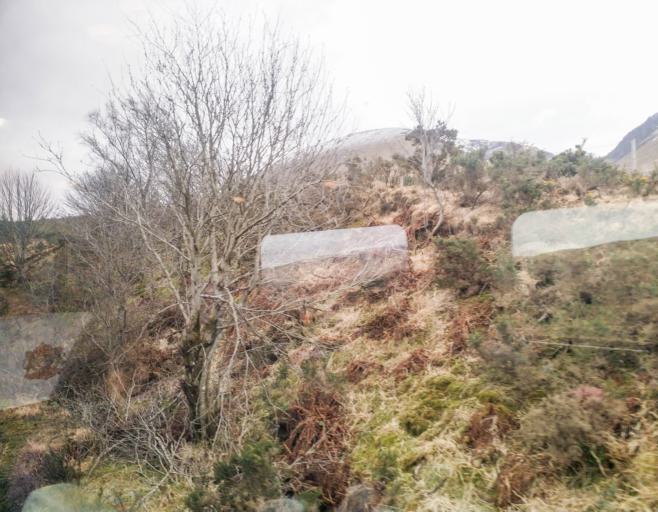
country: GB
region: Scotland
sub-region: Highland
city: Spean Bridge
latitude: 56.5193
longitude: -4.7644
